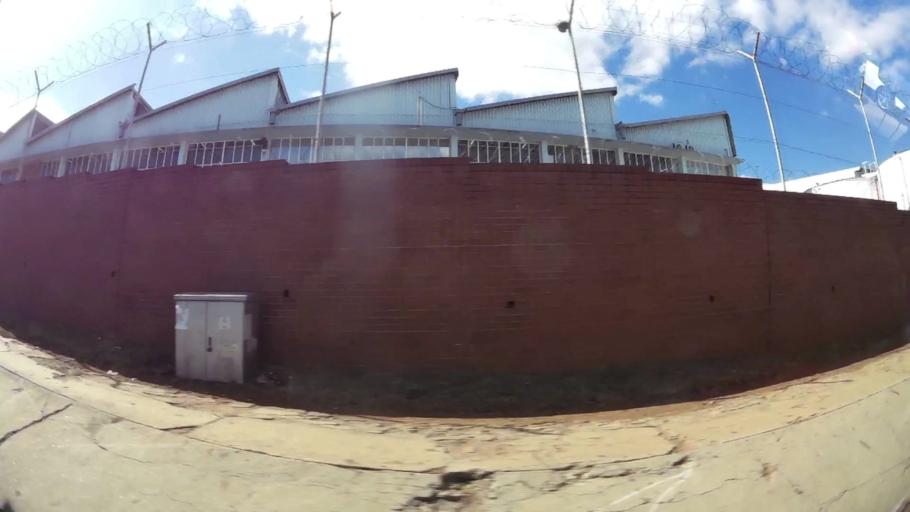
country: ZA
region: Gauteng
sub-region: West Rand District Municipality
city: Krugersdorp
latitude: -26.1165
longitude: 27.8102
